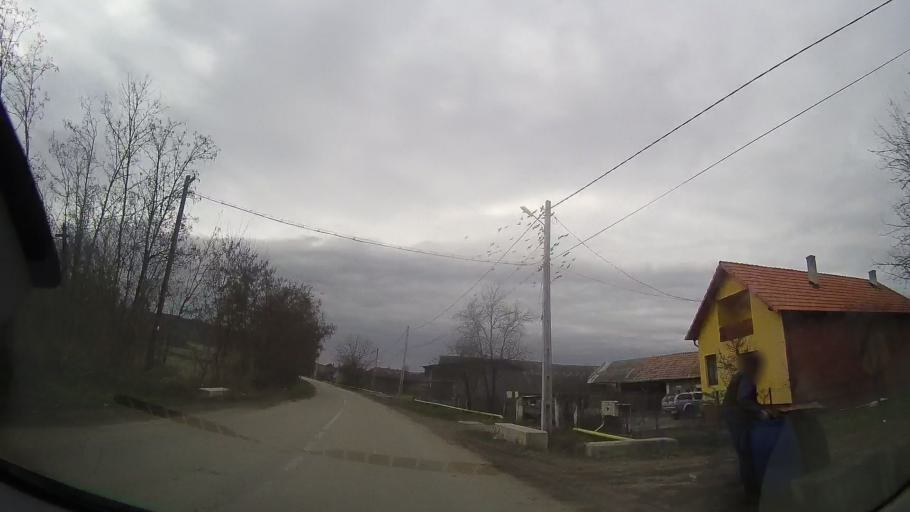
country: RO
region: Bistrita-Nasaud
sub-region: Comuna Milas
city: Milas
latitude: 46.8085
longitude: 24.4277
